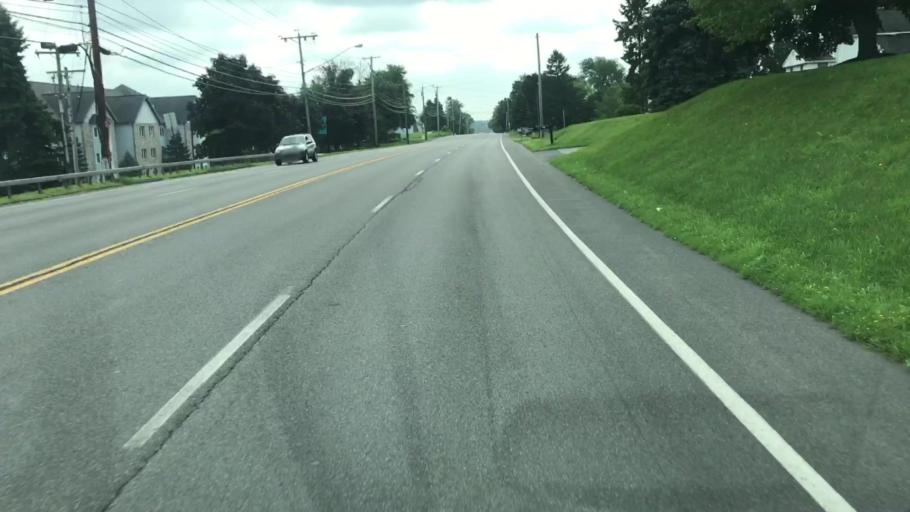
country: US
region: New York
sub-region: Onondaga County
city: Galeville
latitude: 43.0982
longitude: -76.1800
